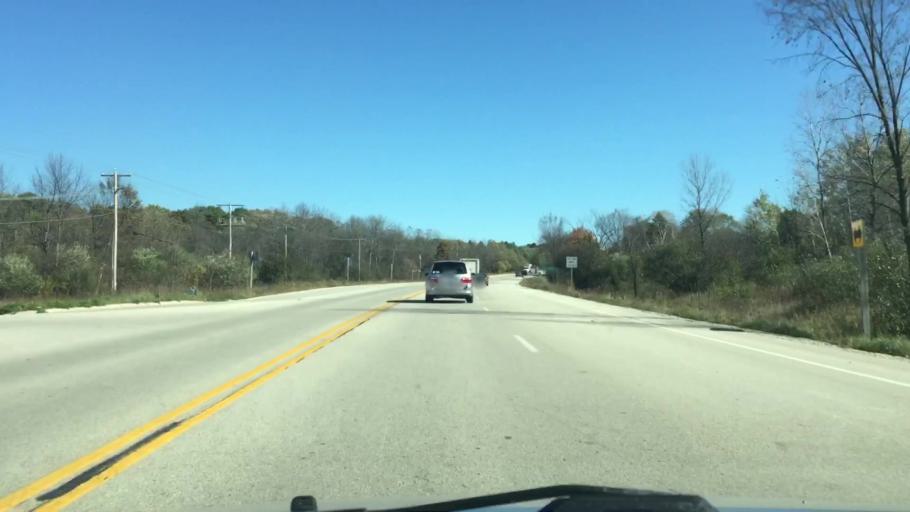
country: US
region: Wisconsin
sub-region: Waukesha County
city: Wales
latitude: 42.9724
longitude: -88.3058
